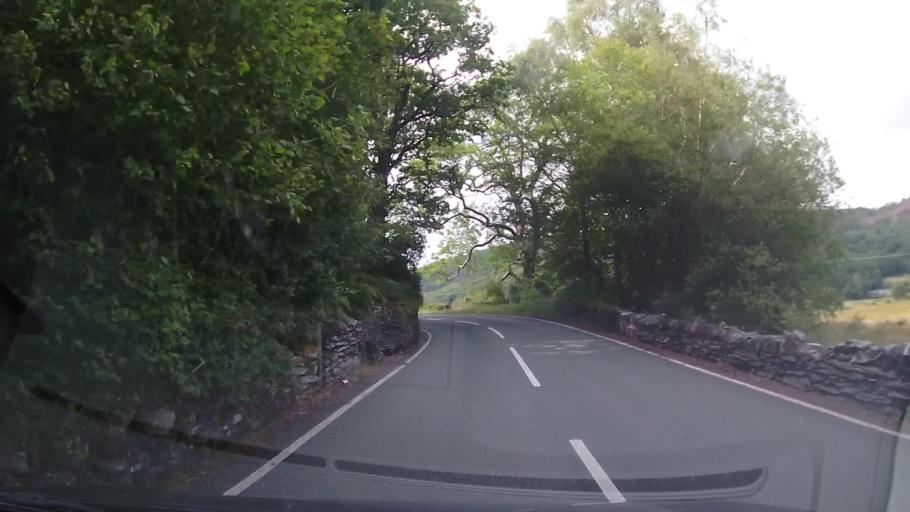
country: GB
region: Wales
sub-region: Gwynedd
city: Maentwrog
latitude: 52.9364
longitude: -4.0214
